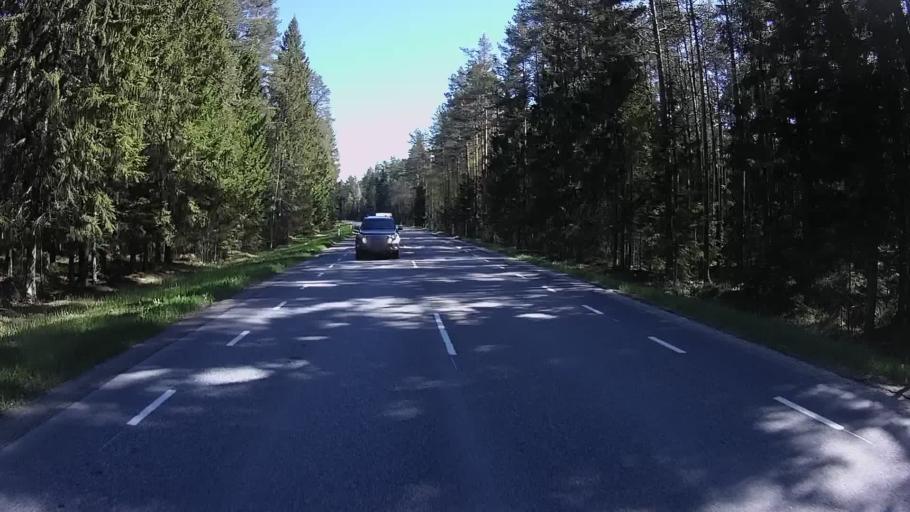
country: EE
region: Harju
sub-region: Loksa linn
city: Loksa
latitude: 59.5564
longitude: 25.7261
